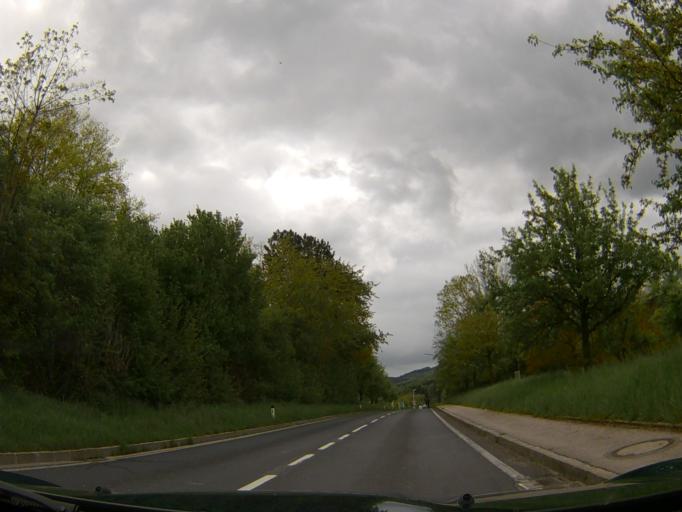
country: AT
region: Upper Austria
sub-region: Politischer Bezirk Vocklabruck
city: Seewalchen
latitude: 47.9438
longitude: 13.5956
